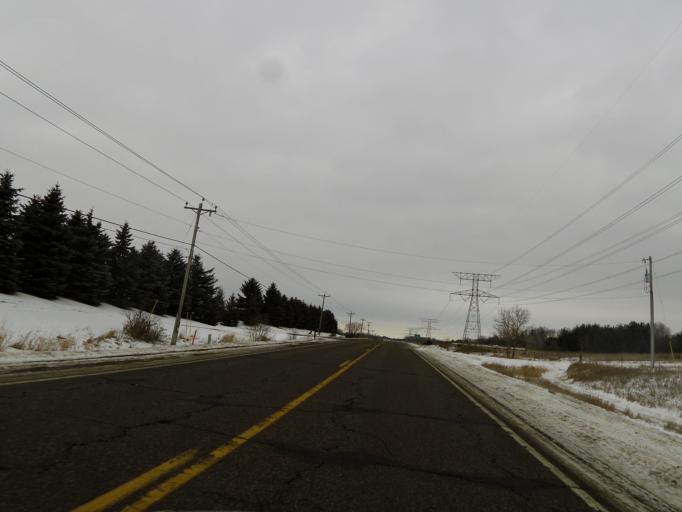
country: US
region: Minnesota
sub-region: Washington County
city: Lake Elmo
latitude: 44.9469
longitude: -92.8361
